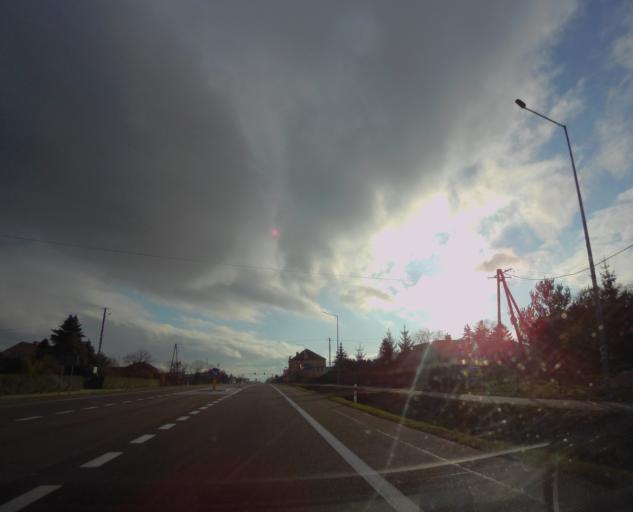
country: PL
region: Subcarpathian Voivodeship
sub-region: Powiat przemyski
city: Orly
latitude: 49.8764
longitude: 22.8126
